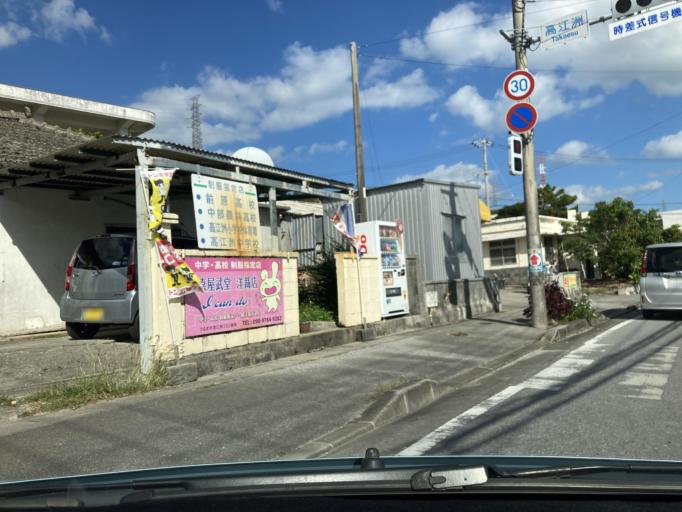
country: JP
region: Okinawa
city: Gushikawa
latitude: 26.3492
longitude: 127.8460
